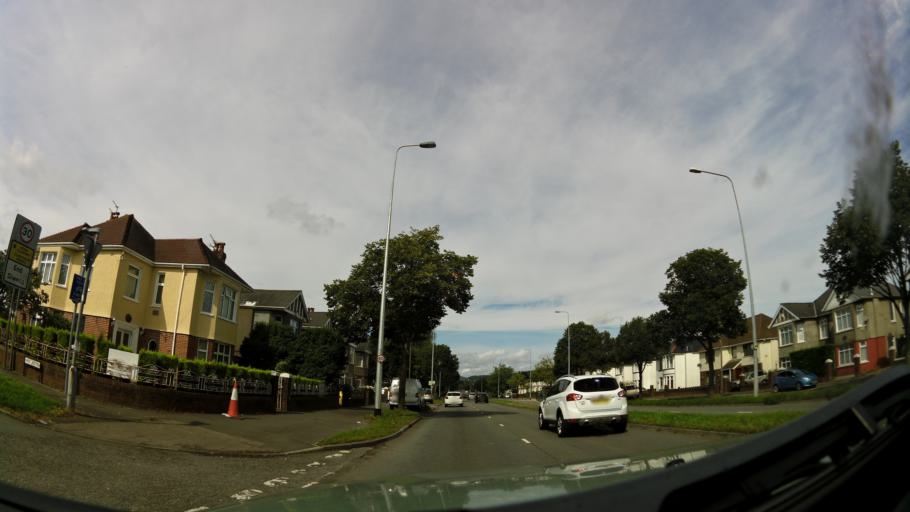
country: GB
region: Wales
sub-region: Cardiff
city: Radyr
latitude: 51.5147
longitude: -3.2121
